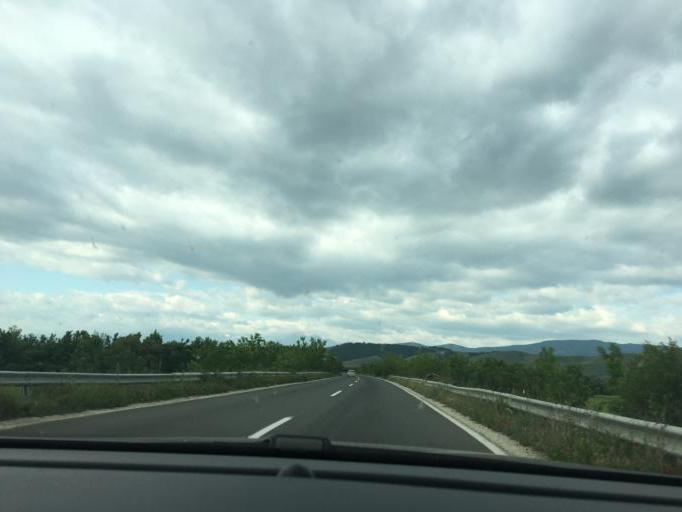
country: MK
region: Prilep
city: Topolcani
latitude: 41.2156
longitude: 21.4265
